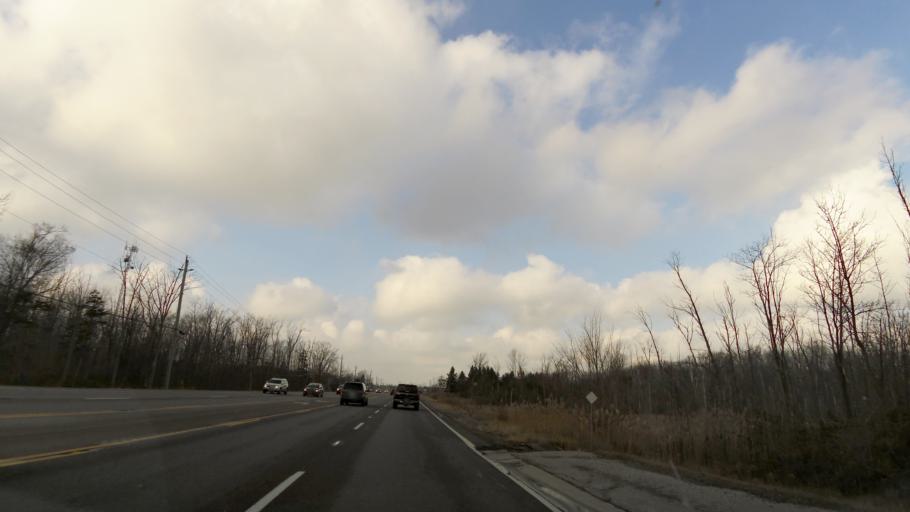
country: CA
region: Ontario
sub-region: Halton
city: Milton
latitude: 43.4132
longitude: -80.0580
